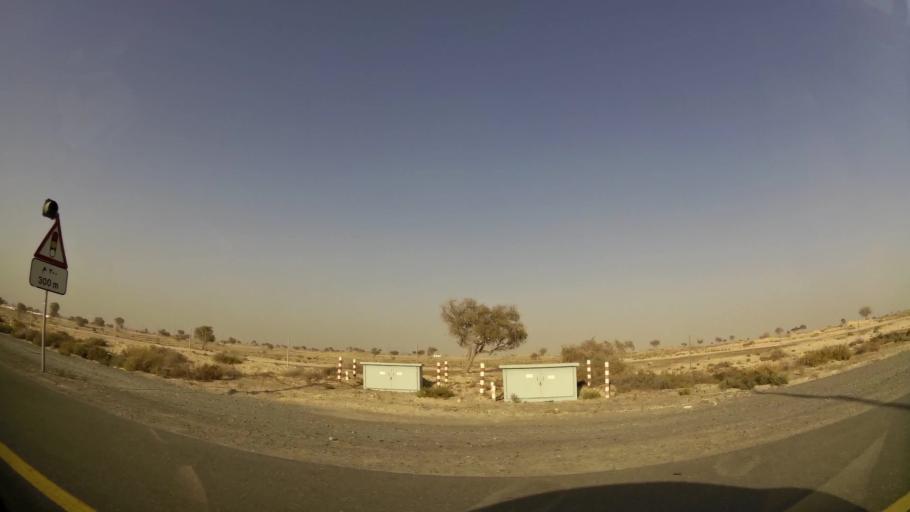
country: AE
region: Dubai
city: Dubai
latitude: 25.0785
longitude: 55.2503
